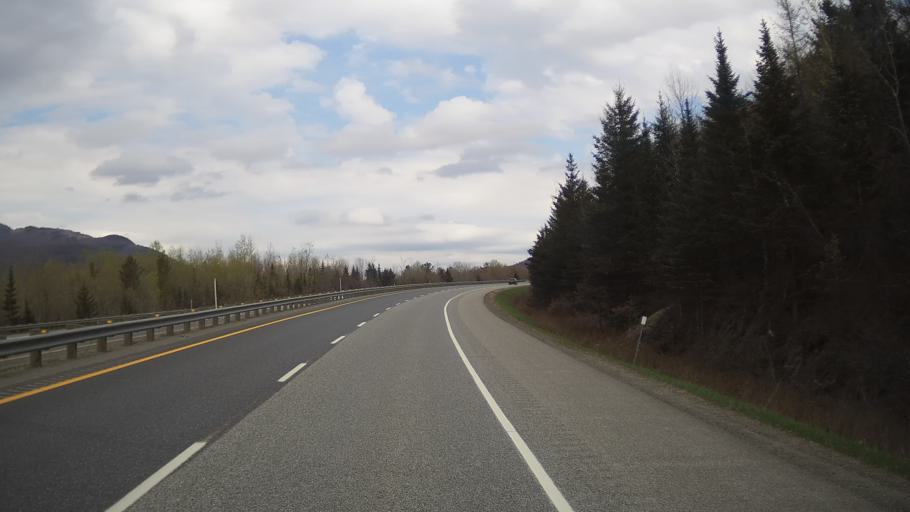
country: CA
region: Quebec
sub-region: Estrie
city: Magog
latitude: 45.2947
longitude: -72.2924
